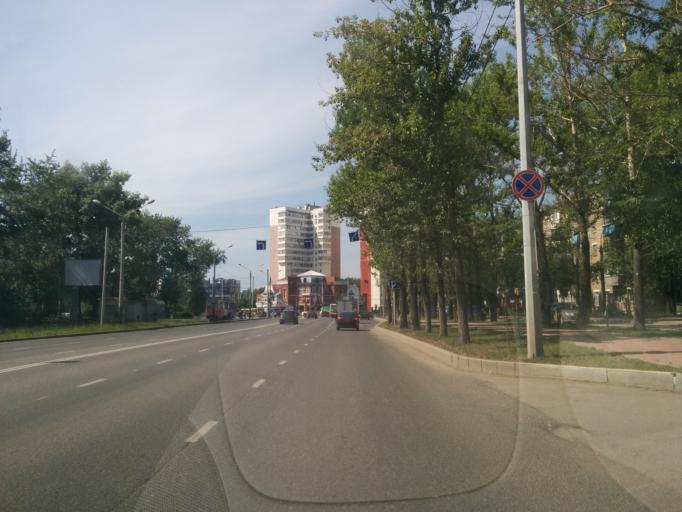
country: RU
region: Perm
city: Perm
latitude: 57.9937
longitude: 56.2898
